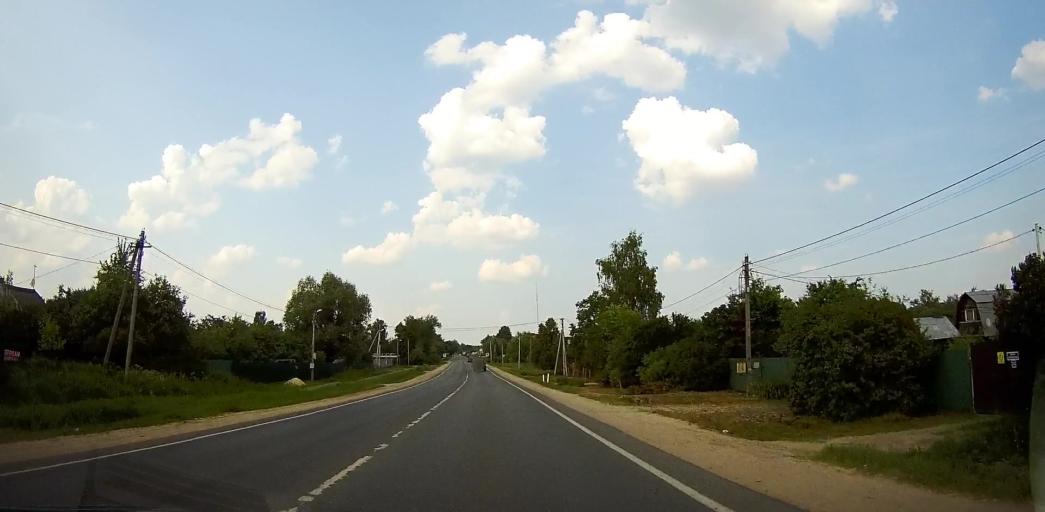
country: RU
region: Moskovskaya
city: Mikhnevo
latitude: 55.1322
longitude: 37.9490
